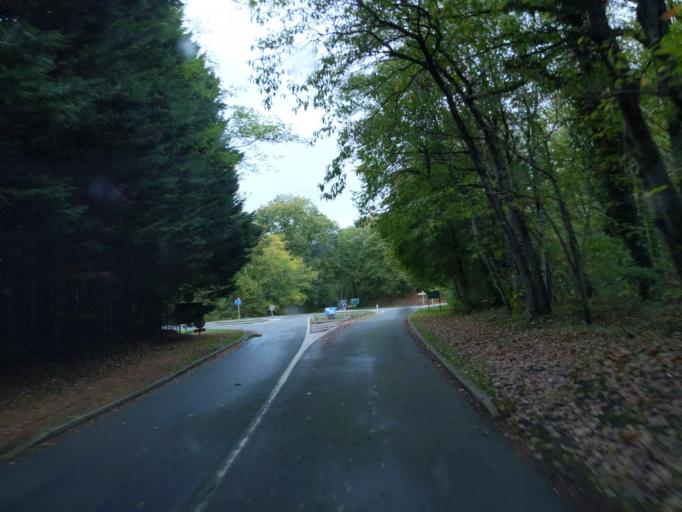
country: FR
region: Ile-de-France
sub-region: Departement des Yvelines
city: Bullion
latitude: 48.5929
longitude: 1.9922
